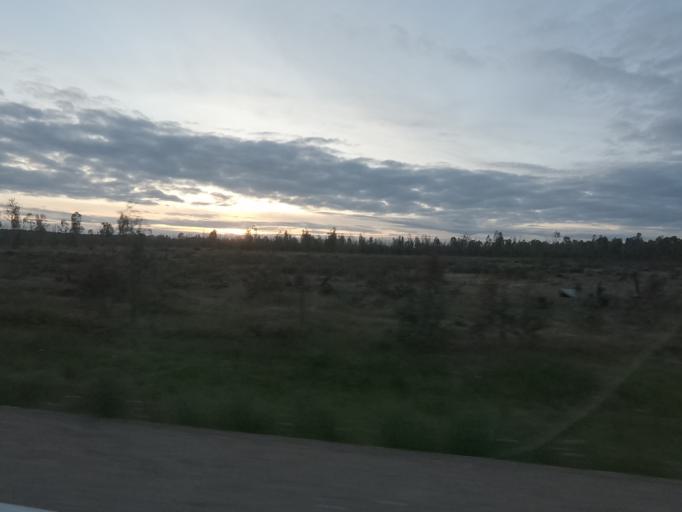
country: ES
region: Extremadura
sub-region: Provincia de Badajoz
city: Badajoz
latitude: 38.9857
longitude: -6.8795
